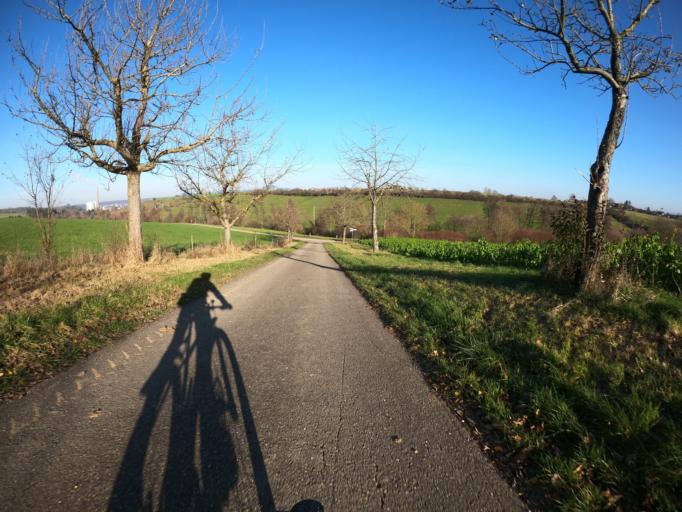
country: DE
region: Baden-Wuerttemberg
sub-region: Regierungsbezirk Stuttgart
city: Eschenbach
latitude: 48.6720
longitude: 9.6743
